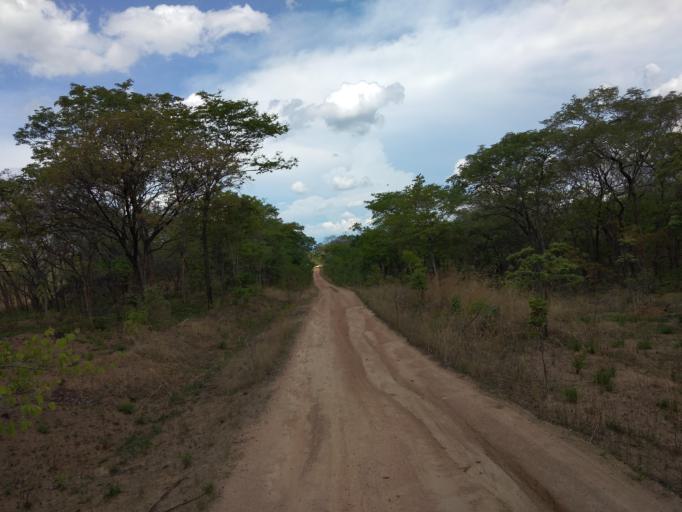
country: ZM
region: Eastern
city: Nyimba
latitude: -14.1269
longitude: 30.0807
